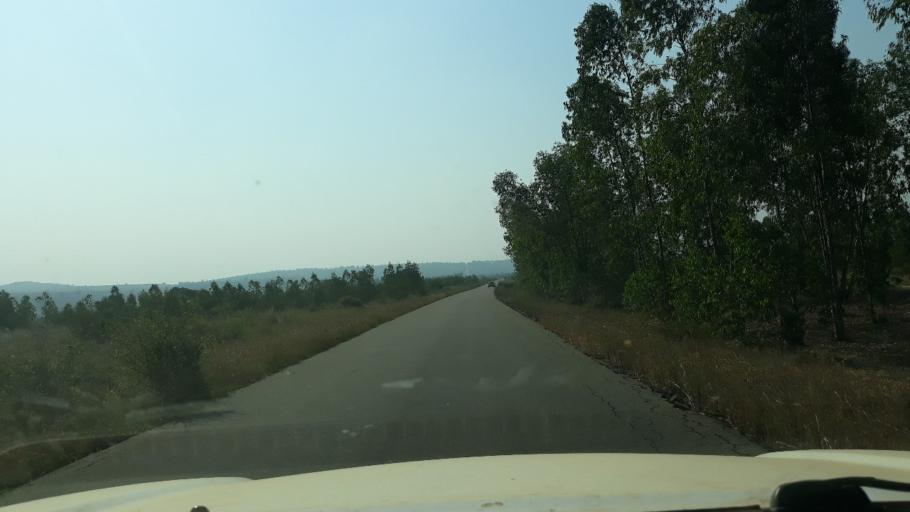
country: BI
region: Cibitoke
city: Cibitoke
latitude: -2.9367
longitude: 29.0660
